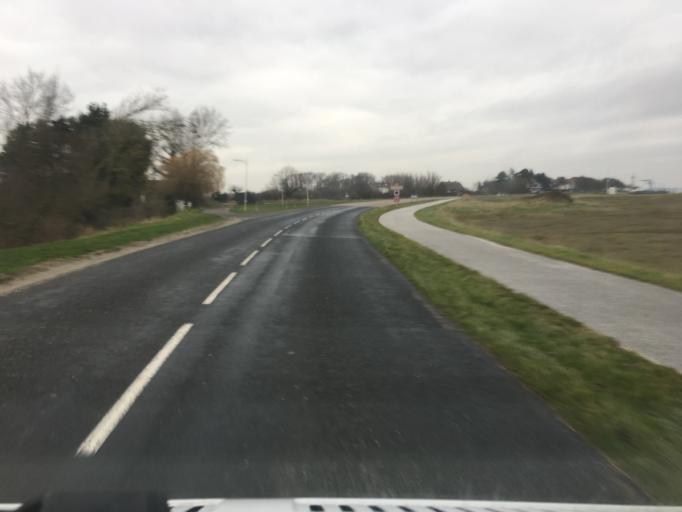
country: FR
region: Picardie
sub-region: Departement de la Somme
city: Pende
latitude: 50.2119
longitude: 1.5588
